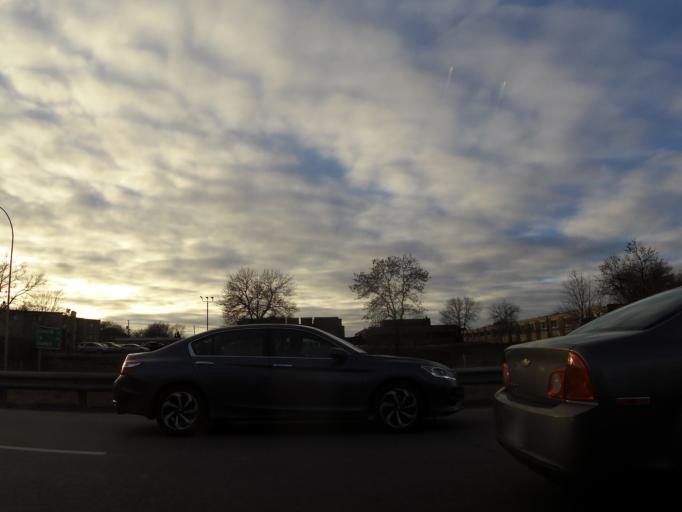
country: US
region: Minnesota
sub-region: Ramsey County
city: New Brighton
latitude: 45.0631
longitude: -93.1863
